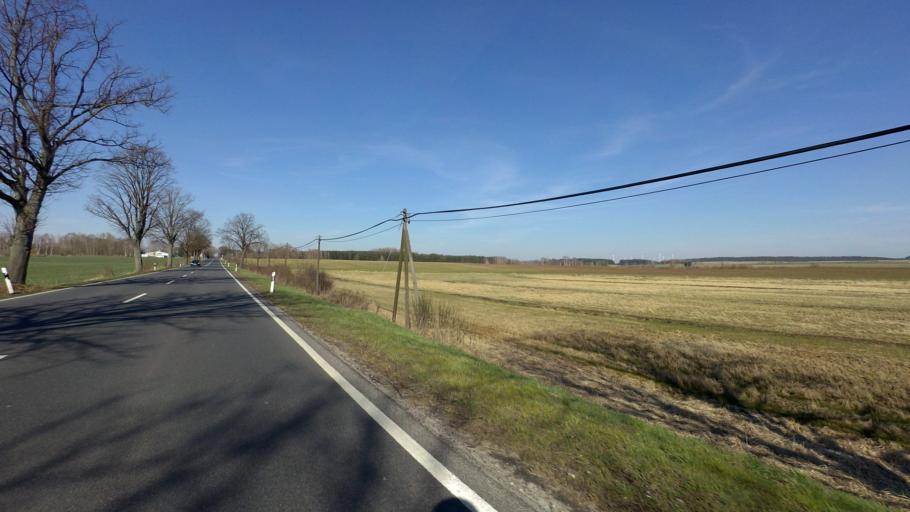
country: DE
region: Brandenburg
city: Angermunde
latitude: 52.9864
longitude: 13.9777
